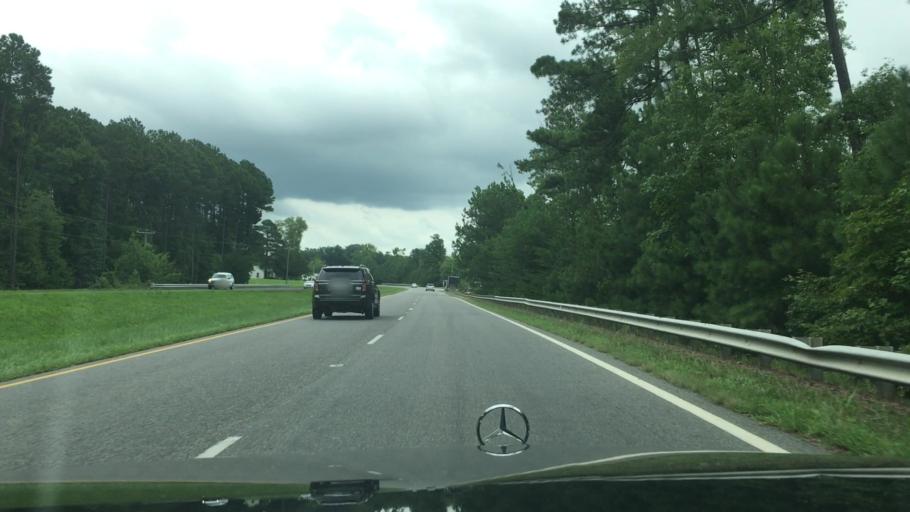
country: US
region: Virginia
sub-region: Chesterfield County
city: Woodlake
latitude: 37.3877
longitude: -77.7584
